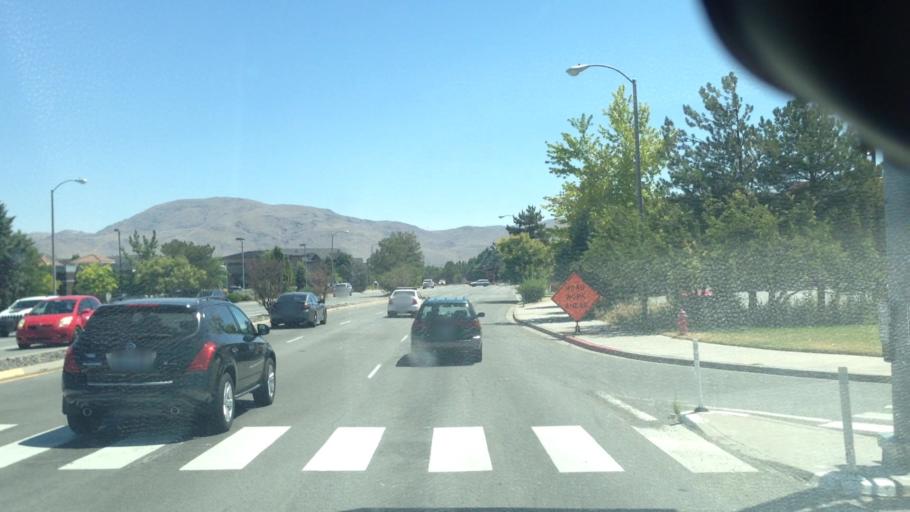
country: US
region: Nevada
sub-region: Washoe County
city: Sparks
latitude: 39.4387
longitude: -119.7584
